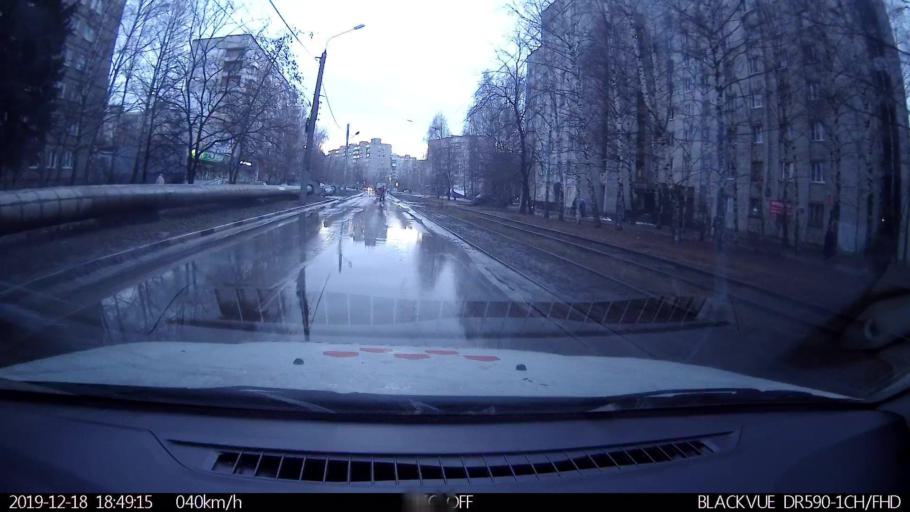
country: RU
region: Nizjnij Novgorod
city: Nizhniy Novgorod
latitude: 56.3353
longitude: 43.8740
